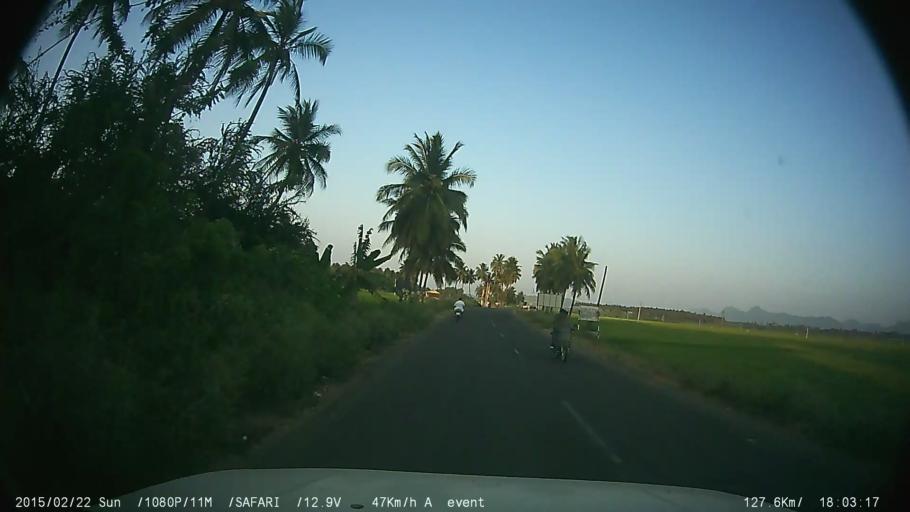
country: IN
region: Tamil Nadu
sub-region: Theni
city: Uttamapalaiyam
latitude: 9.8095
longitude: 77.3419
